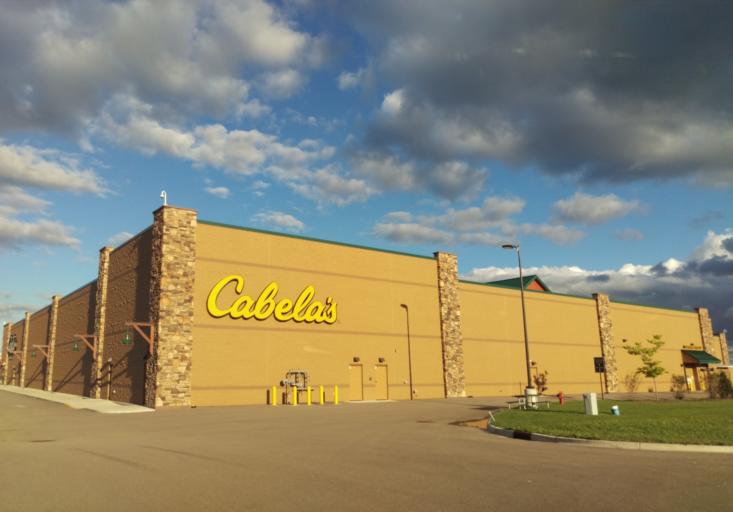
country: US
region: Wisconsin
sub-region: Dane County
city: Sun Prairie
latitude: 43.1647
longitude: -89.2741
